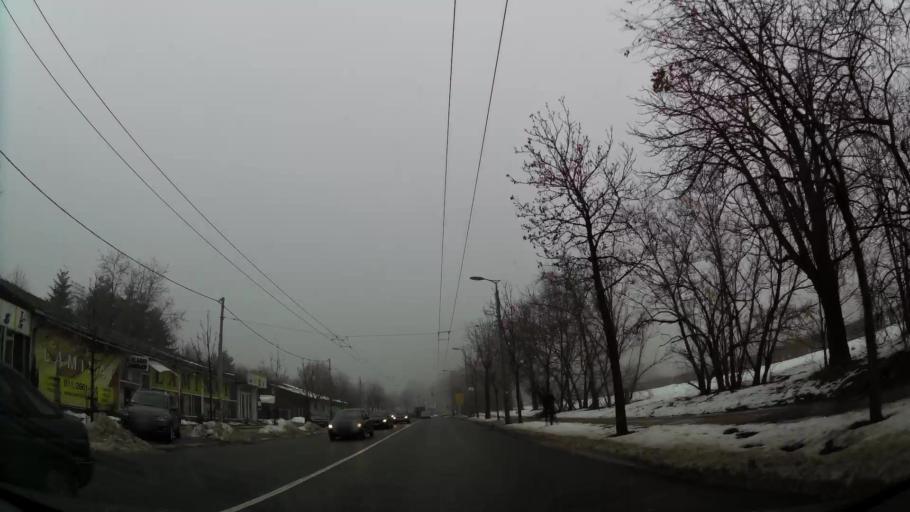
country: RS
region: Central Serbia
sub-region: Belgrade
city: Vozdovac
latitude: 44.7623
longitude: 20.4732
